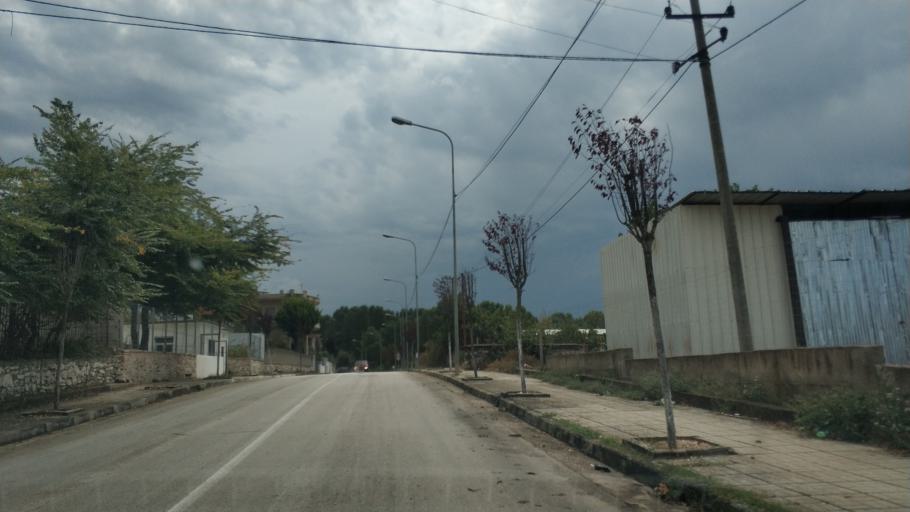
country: AL
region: Vlore
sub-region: Rrethi i Sarandes
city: Sarande
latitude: 39.8440
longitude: 20.0342
